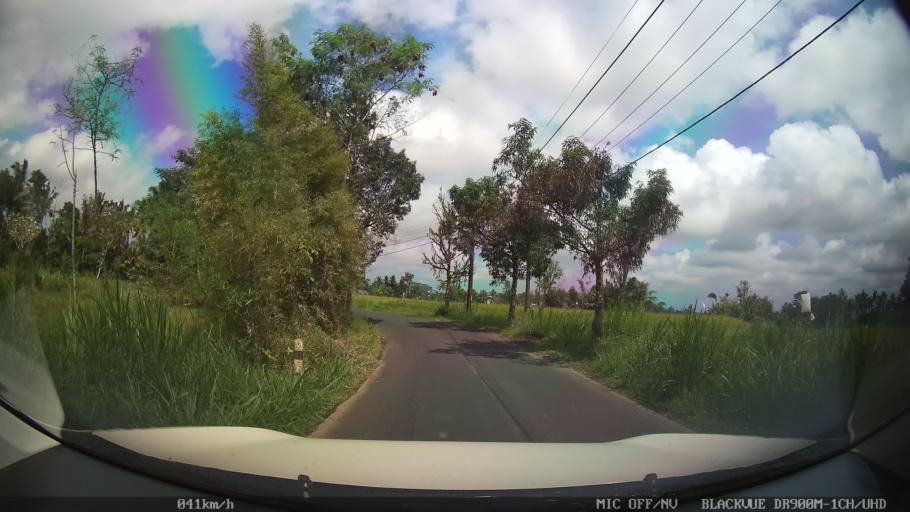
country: ID
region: Bali
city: Banjar Abuan
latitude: -8.4621
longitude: 115.3239
